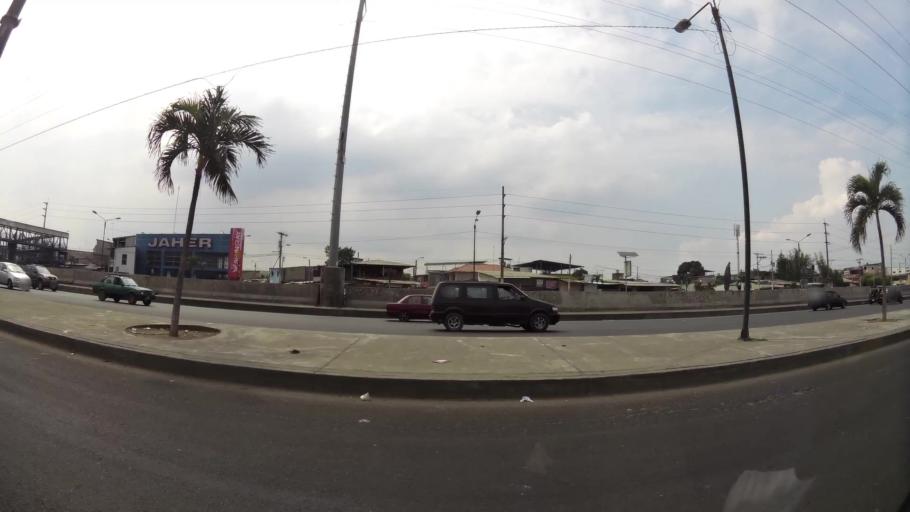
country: EC
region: Guayas
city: Guayaquil
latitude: -2.2402
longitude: -79.9195
